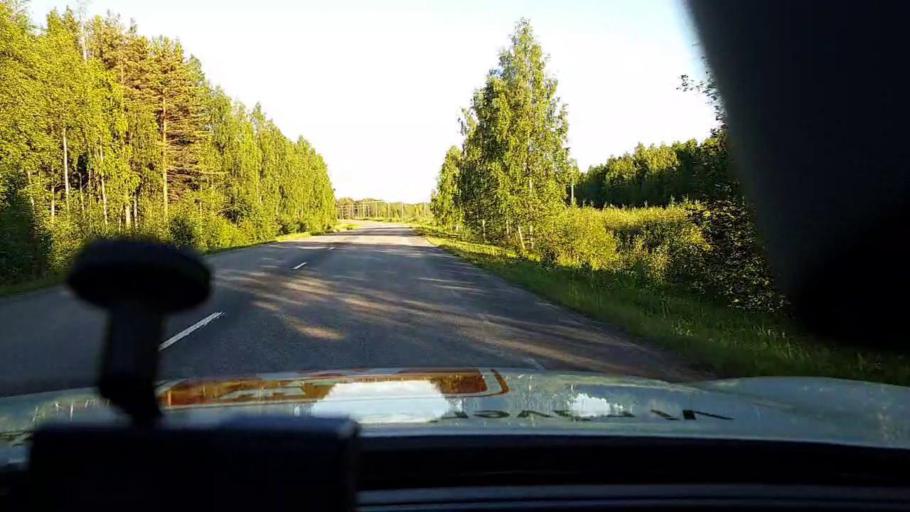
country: SE
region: Norrbotten
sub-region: Lulea Kommun
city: Lulea
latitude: 65.6106
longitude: 22.1646
